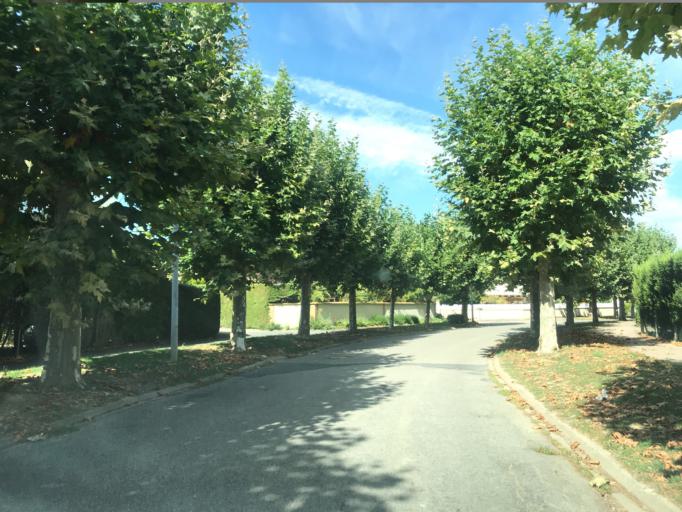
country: FR
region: Haute-Normandie
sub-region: Departement de l'Eure
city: Gaillon
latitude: 49.1610
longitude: 1.3439
